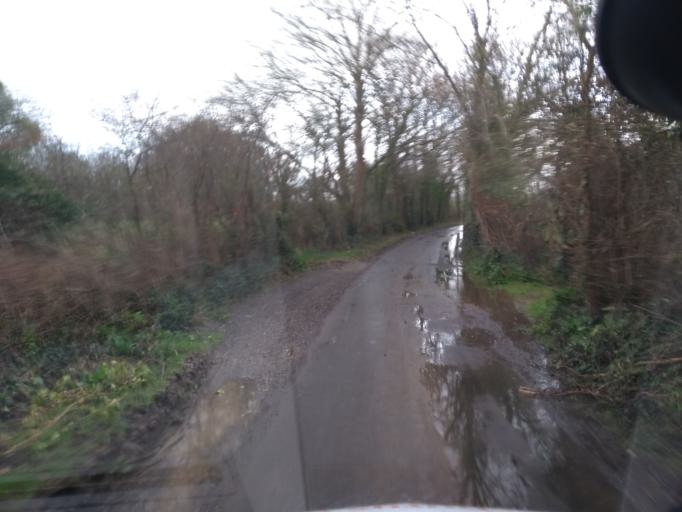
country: GB
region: England
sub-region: Somerset
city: South Petherton
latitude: 50.9757
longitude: -2.8153
